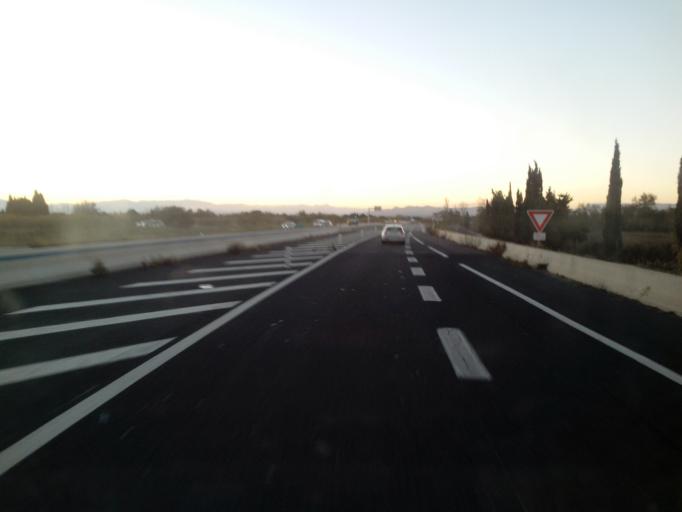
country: FR
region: Languedoc-Roussillon
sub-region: Departement des Pyrenees-Orientales
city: Le Barcares
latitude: 42.7868
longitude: 3.0144
